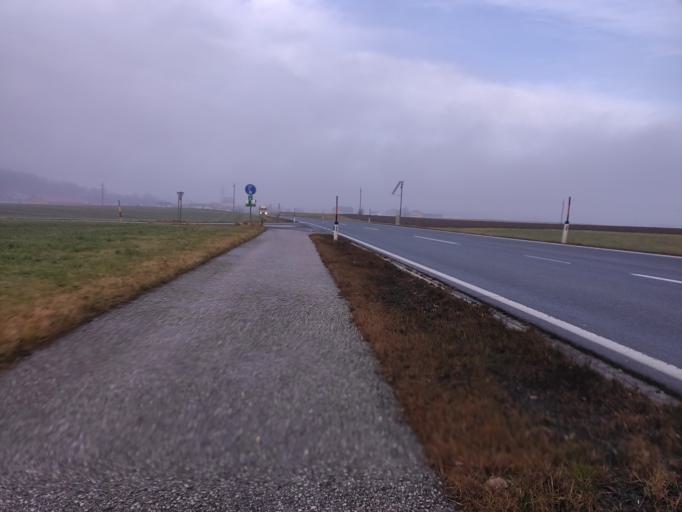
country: AT
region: Upper Austria
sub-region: Politischer Bezirk Vocklabruck
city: Oberhofen am Irrsee
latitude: 47.9648
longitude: 13.2917
